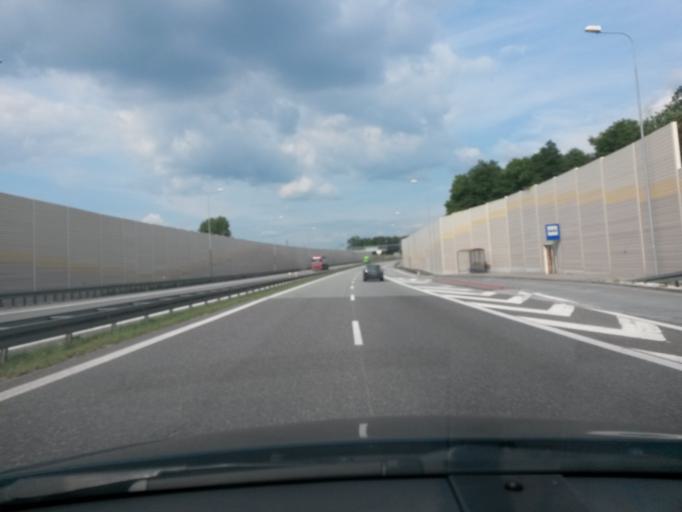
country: PL
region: Lodz Voivodeship
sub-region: Powiat skierniewicki
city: Kowiesy
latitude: 51.8394
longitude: 20.3482
